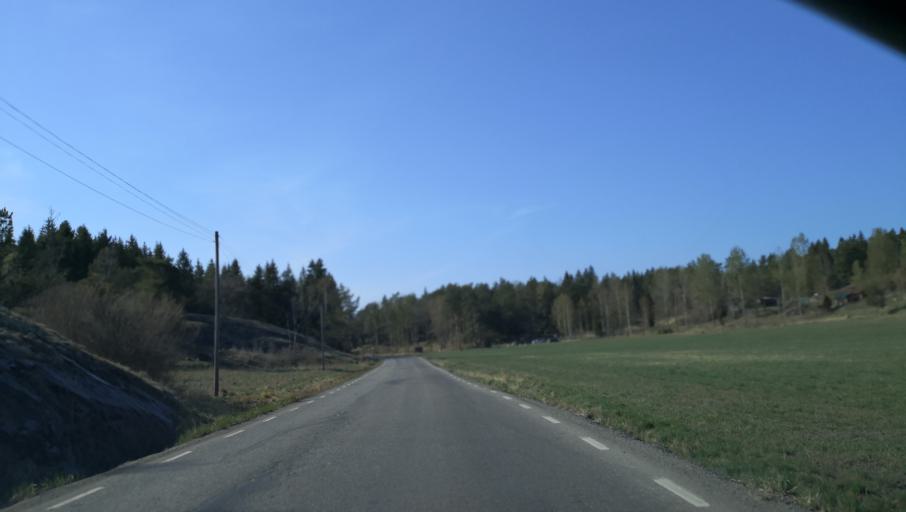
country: SE
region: Stockholm
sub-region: Varmdo Kommun
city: Holo
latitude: 59.3022
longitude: 18.5981
